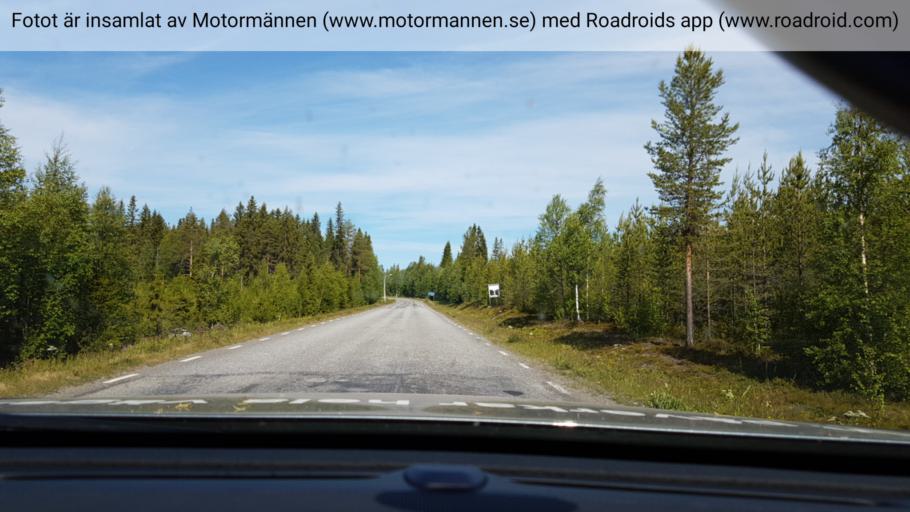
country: SE
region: Vaesterbotten
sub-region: Dorotea Kommun
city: Dorotea
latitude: 64.4043
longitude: 16.0569
